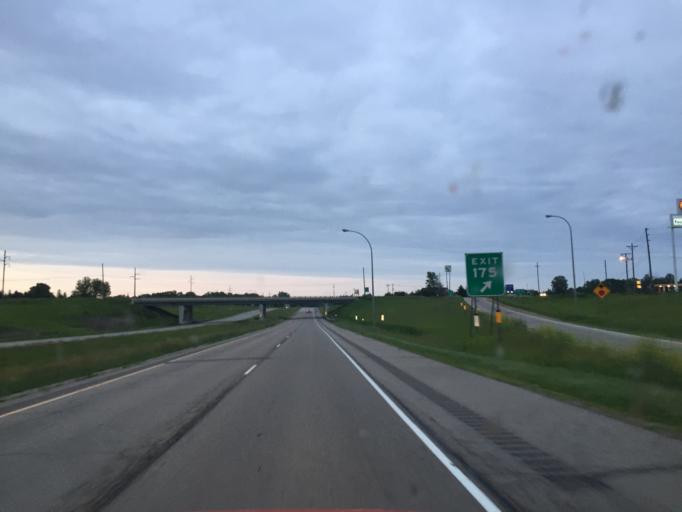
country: US
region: Minnesota
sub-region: Mower County
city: Austin
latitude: 43.6653
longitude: -93.0213
